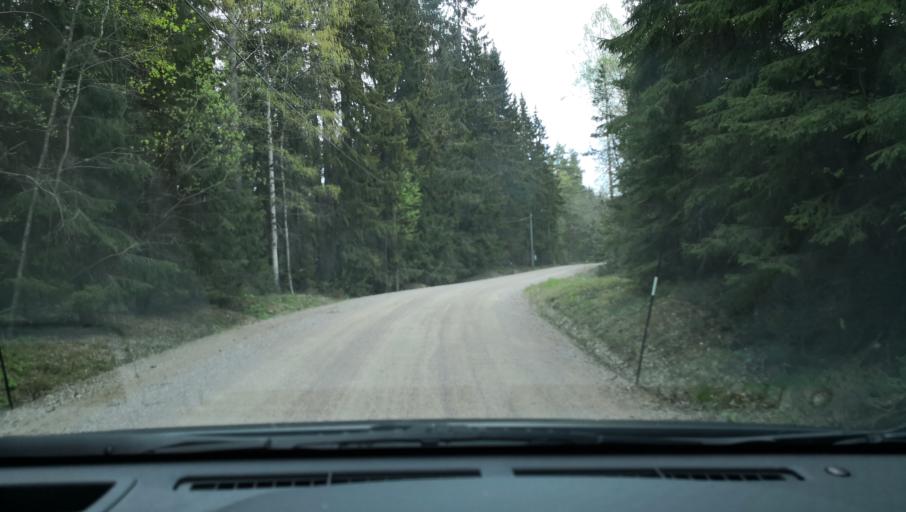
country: SE
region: Vaestmanland
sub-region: Fagersta Kommun
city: Fagersta
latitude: 60.0943
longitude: 15.7899
